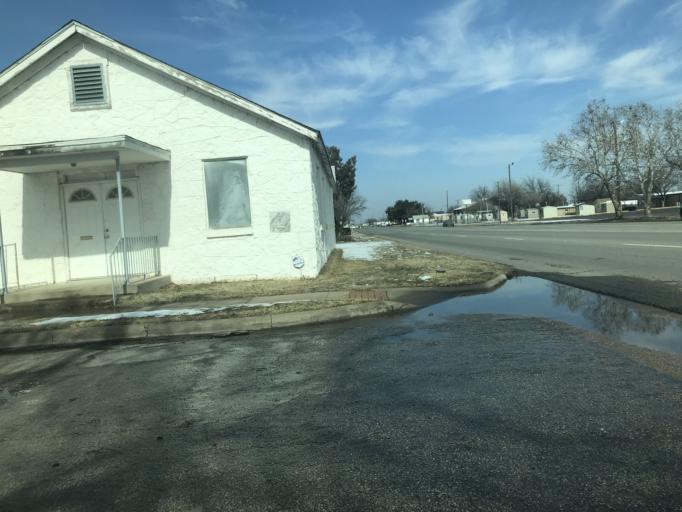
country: US
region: Texas
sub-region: Taylor County
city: Abilene
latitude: 32.4569
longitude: -99.7261
